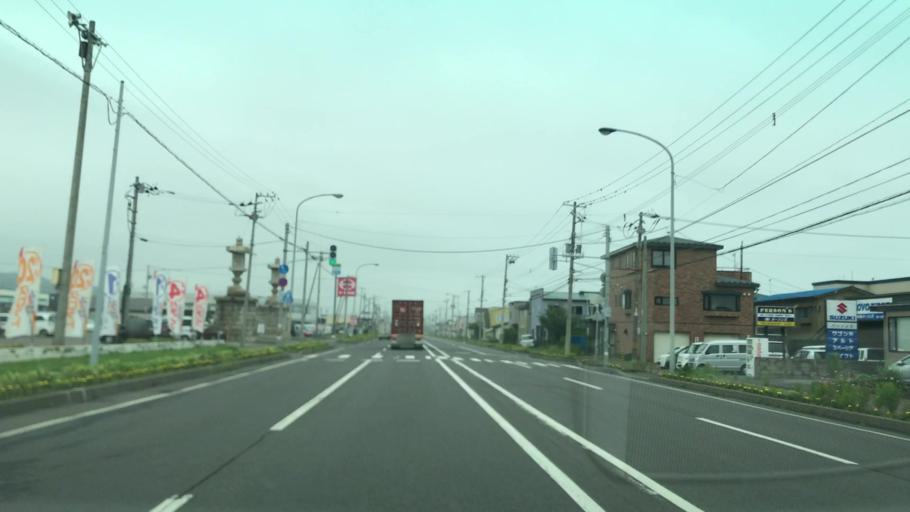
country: JP
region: Hokkaido
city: Muroran
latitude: 42.3711
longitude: 141.0640
